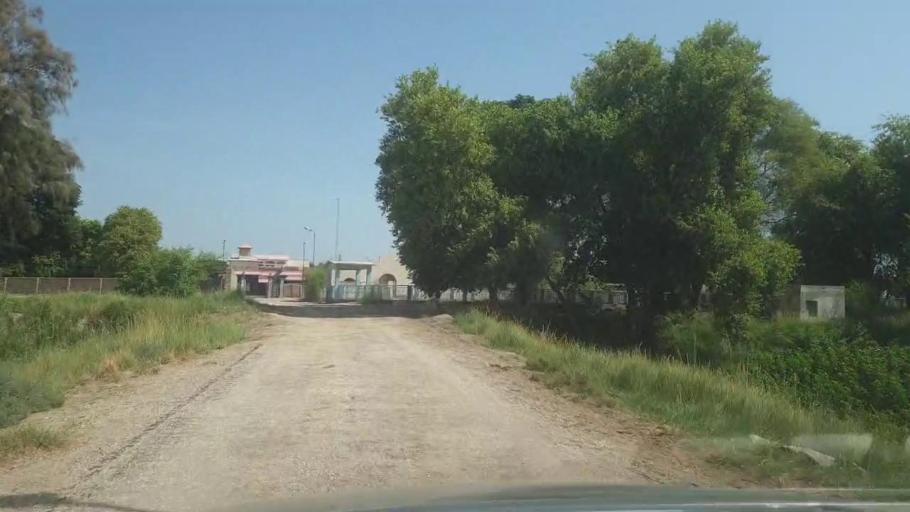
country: PK
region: Sindh
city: Rohri
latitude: 27.4054
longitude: 69.0813
